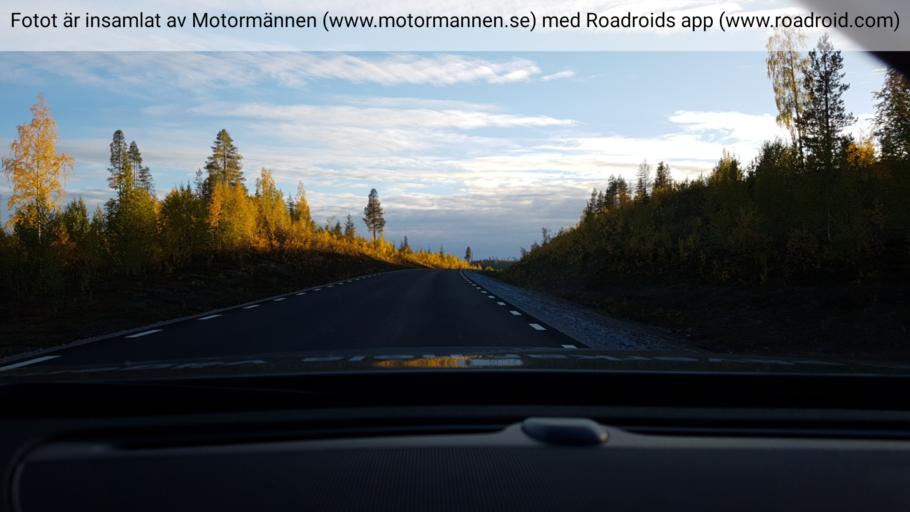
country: SE
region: Norrbotten
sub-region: Jokkmokks Kommun
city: Jokkmokk
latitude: 66.5706
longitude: 19.7997
